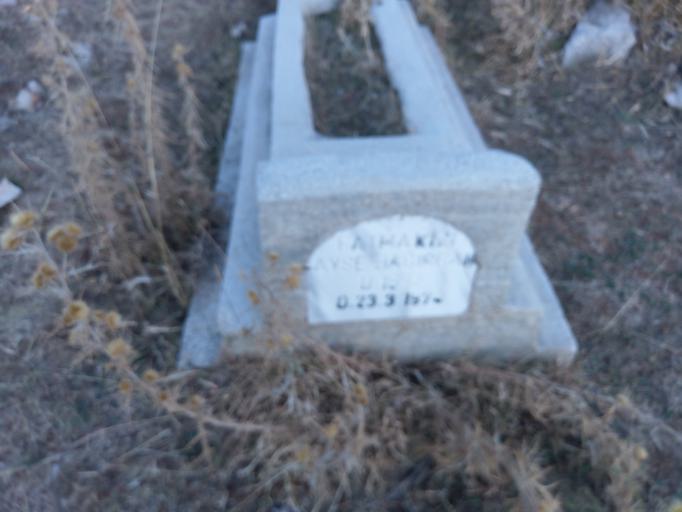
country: TR
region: Kayseri
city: Toklar
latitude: 38.3812
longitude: 36.1390
